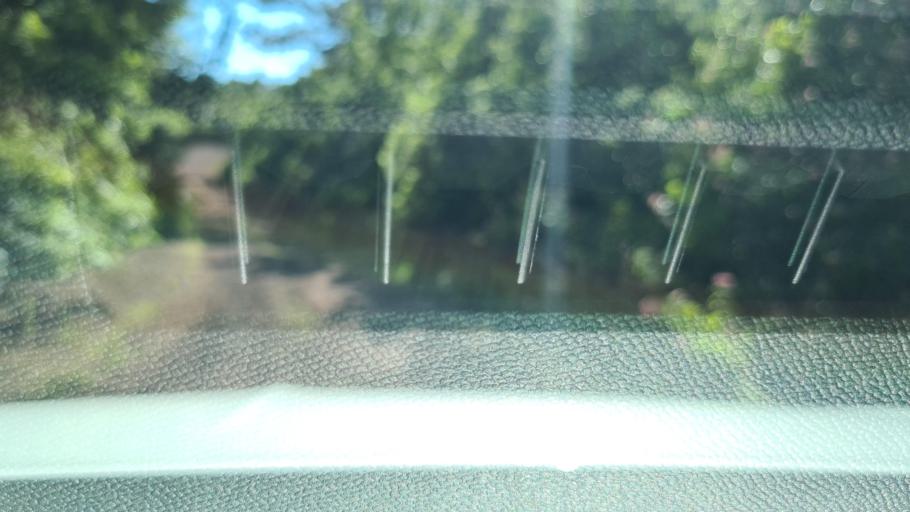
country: PT
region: Azores
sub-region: Sao Roque do Pico
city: Sao Roque do Pico
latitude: 38.4129
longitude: -28.3119
